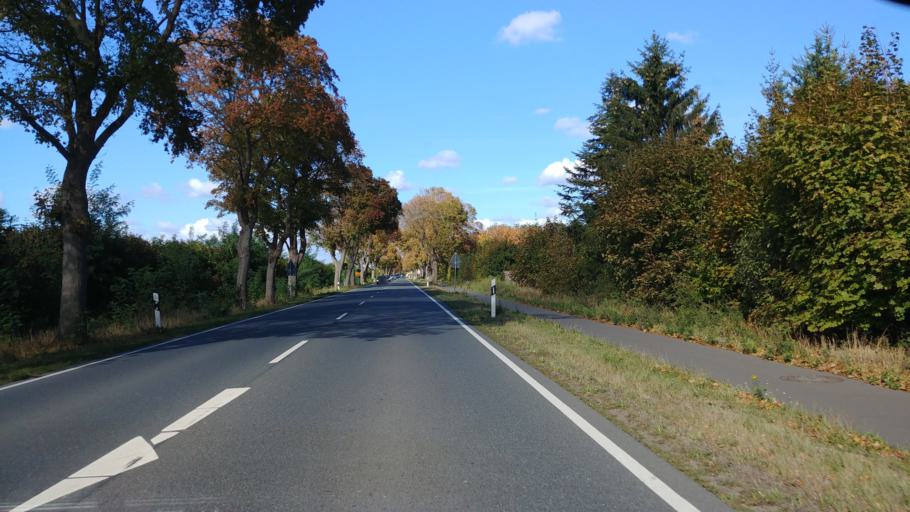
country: DE
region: Lower Saxony
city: Didderse
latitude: 52.3702
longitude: 10.3871
